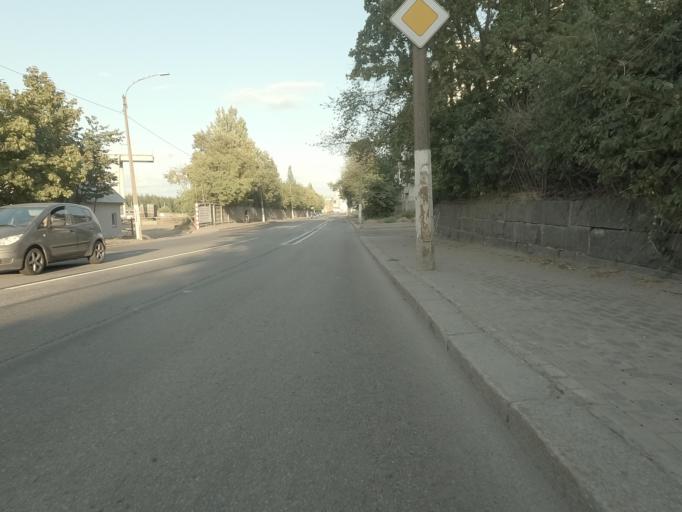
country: RU
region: Leningrad
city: Vyborg
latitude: 60.7111
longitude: 28.7649
